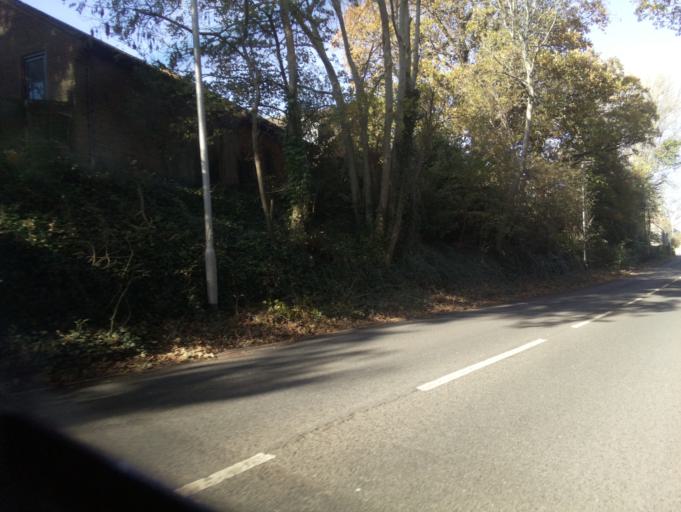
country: GB
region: England
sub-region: Somerset
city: Yeovil
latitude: 50.9489
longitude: -2.6396
